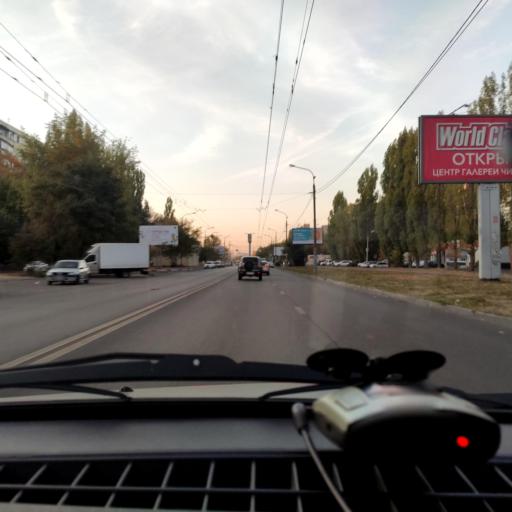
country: RU
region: Voronezj
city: Podgornoye
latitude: 51.7035
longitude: 39.1482
